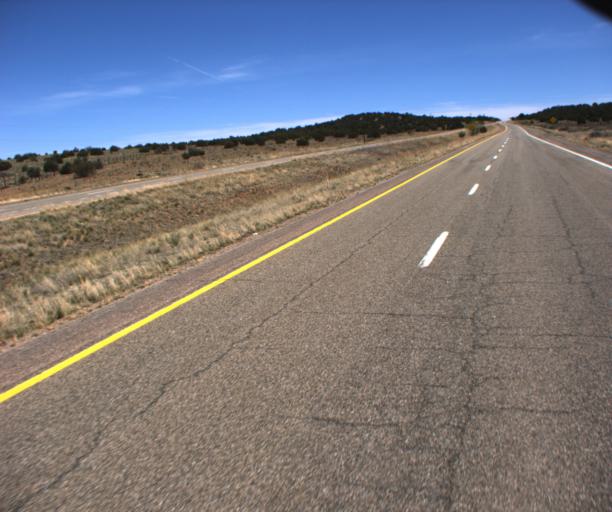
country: US
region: Arizona
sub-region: Mohave County
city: Peach Springs
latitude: 35.5295
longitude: -113.2297
